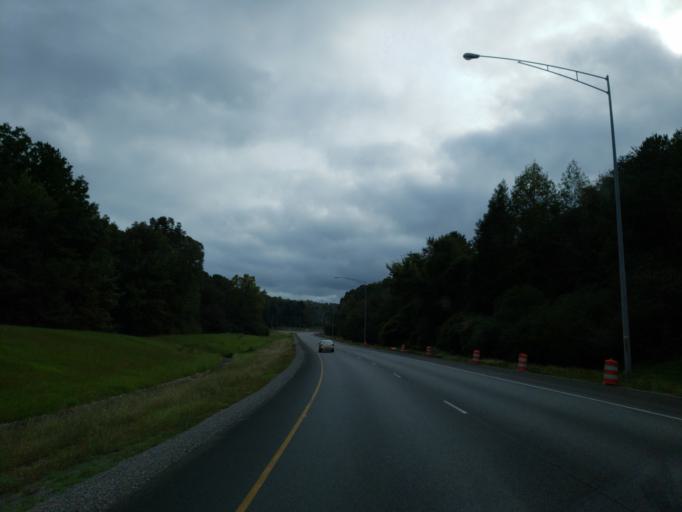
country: US
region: Alabama
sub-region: Jefferson County
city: Bessemer
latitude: 33.3397
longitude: -87.0338
